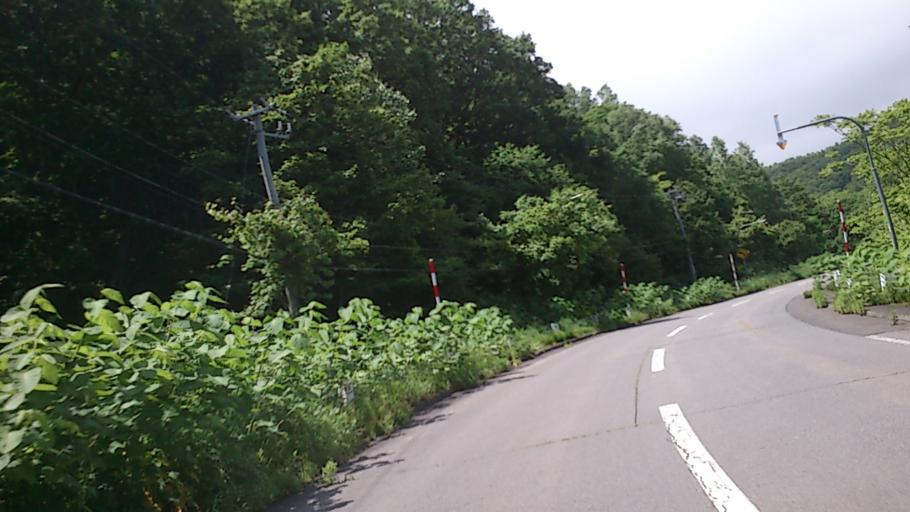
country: JP
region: Hokkaido
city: Niseko Town
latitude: 42.8228
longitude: 140.5274
